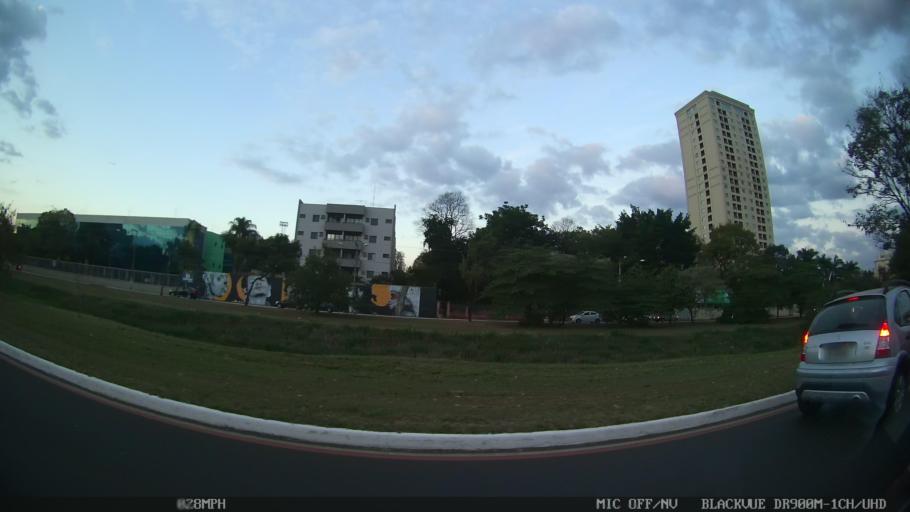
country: BR
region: Sao Paulo
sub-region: Ribeirao Preto
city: Ribeirao Preto
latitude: -21.2053
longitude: -47.7925
